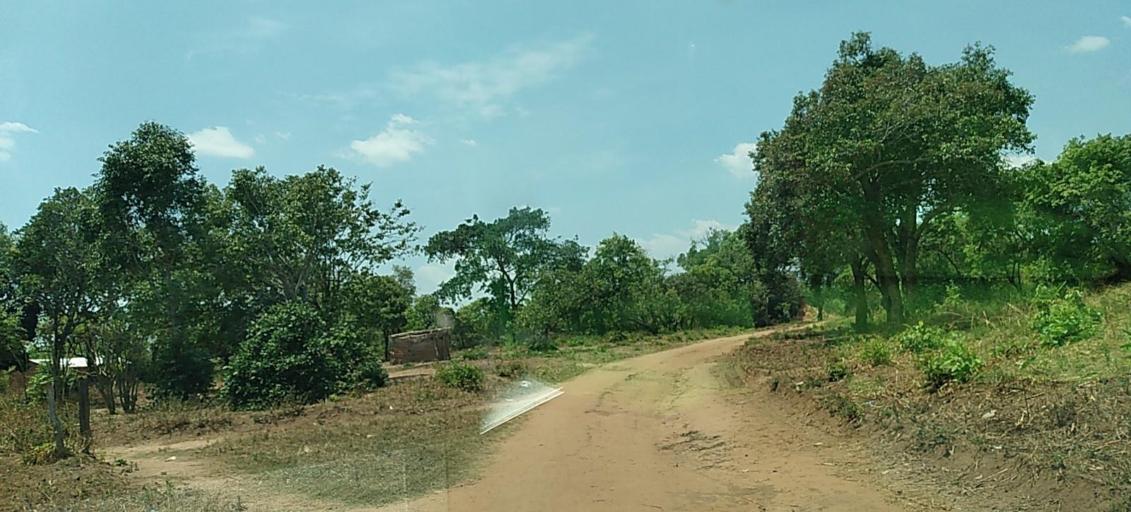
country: CD
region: Katanga
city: Kolwezi
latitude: -11.3204
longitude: 25.2300
